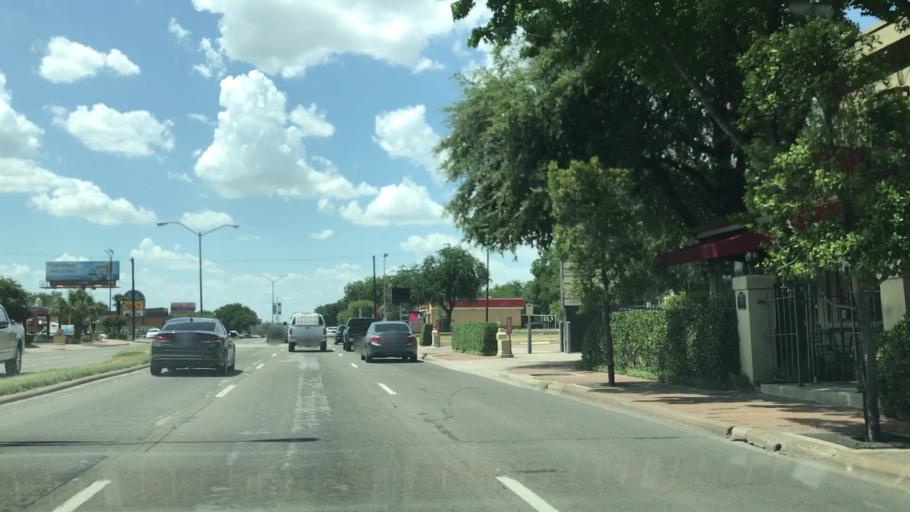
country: US
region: Texas
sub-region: Dallas County
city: Highland Park
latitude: 32.8131
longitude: -96.8068
